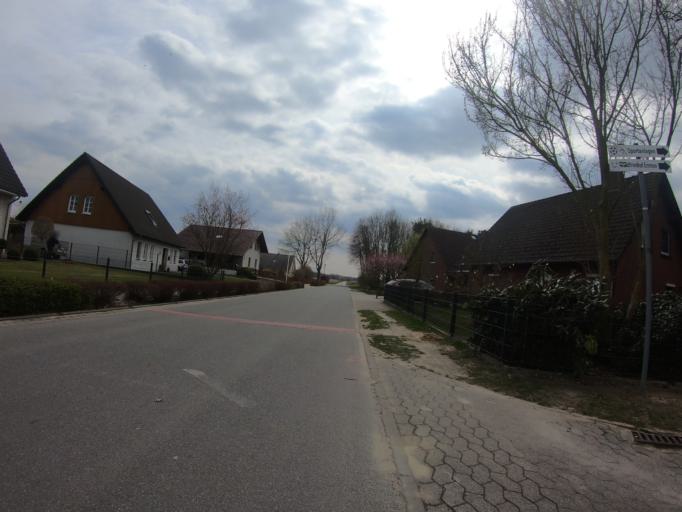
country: DE
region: Lower Saxony
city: Hankensbuttel
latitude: 52.7091
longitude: 10.6210
